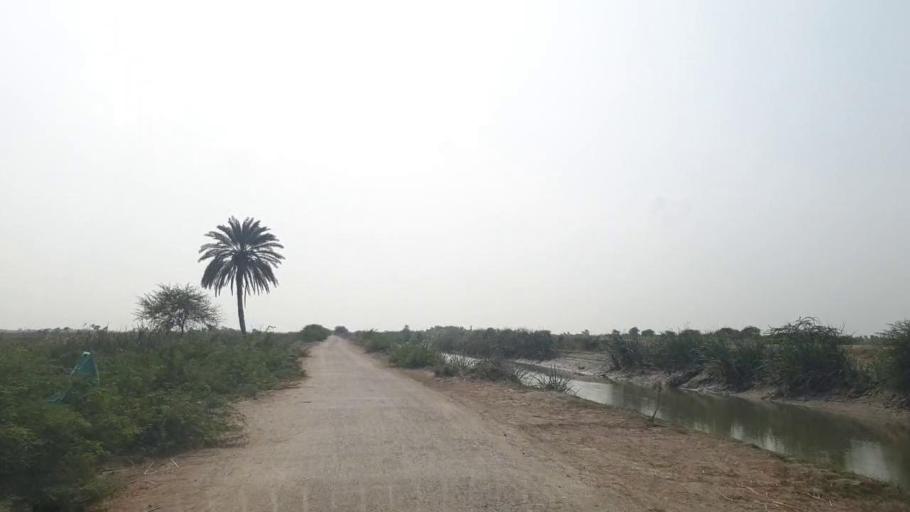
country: PK
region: Sindh
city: Badin
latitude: 24.7246
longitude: 68.7347
